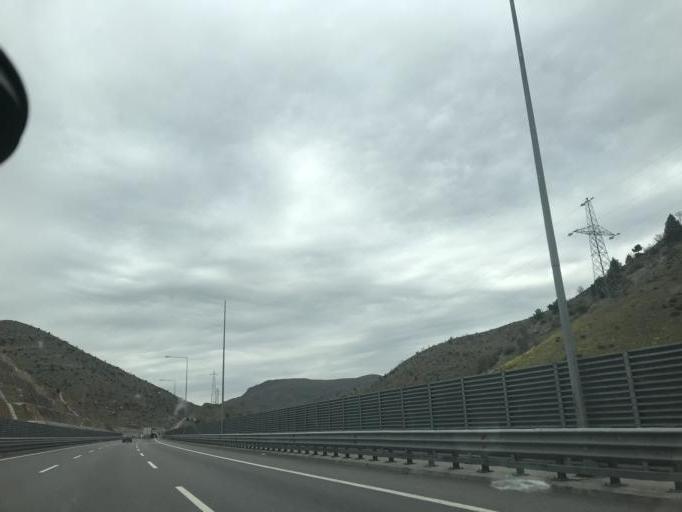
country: TR
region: Nigde
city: Ciftehan
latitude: 37.5673
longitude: 34.7554
